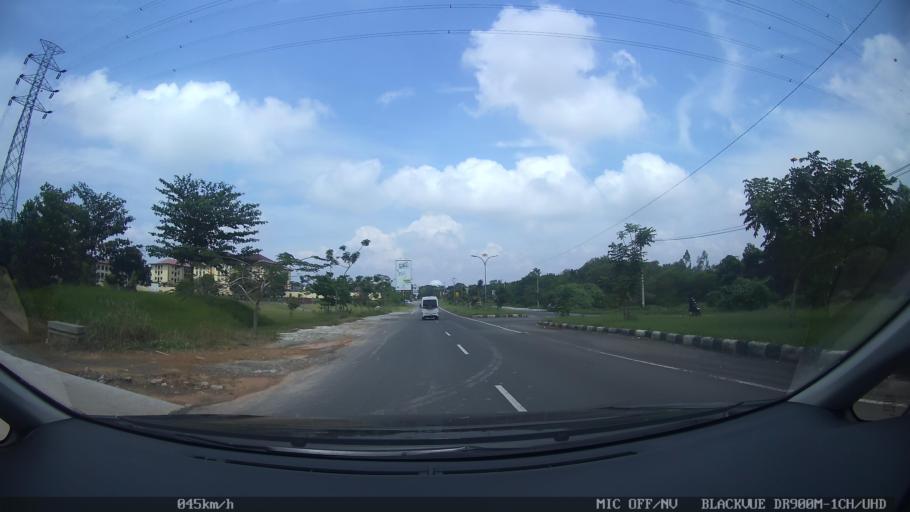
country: ID
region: Lampung
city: Kedaton
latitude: -5.3582
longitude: 105.3090
